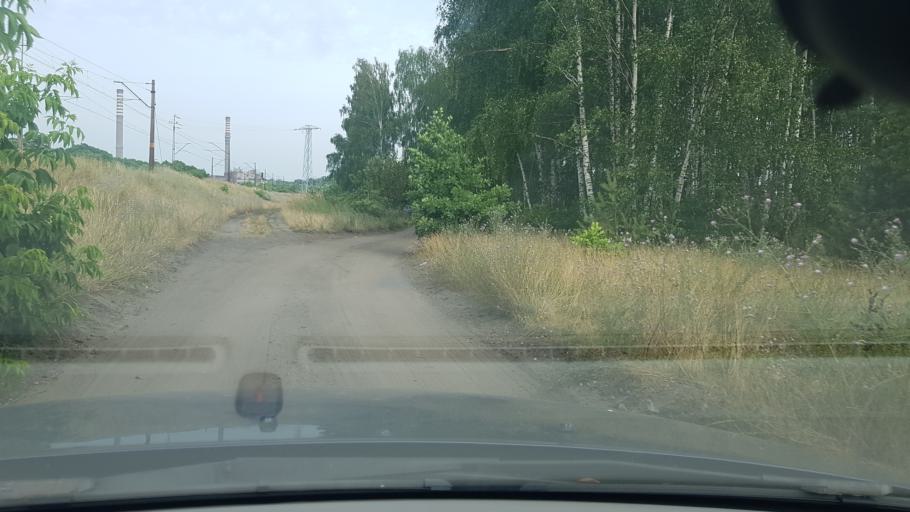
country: PL
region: Lodz Voivodeship
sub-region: Powiat tomaszowski
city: Tomaszow Mazowiecki
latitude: 51.5530
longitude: 20.0231
